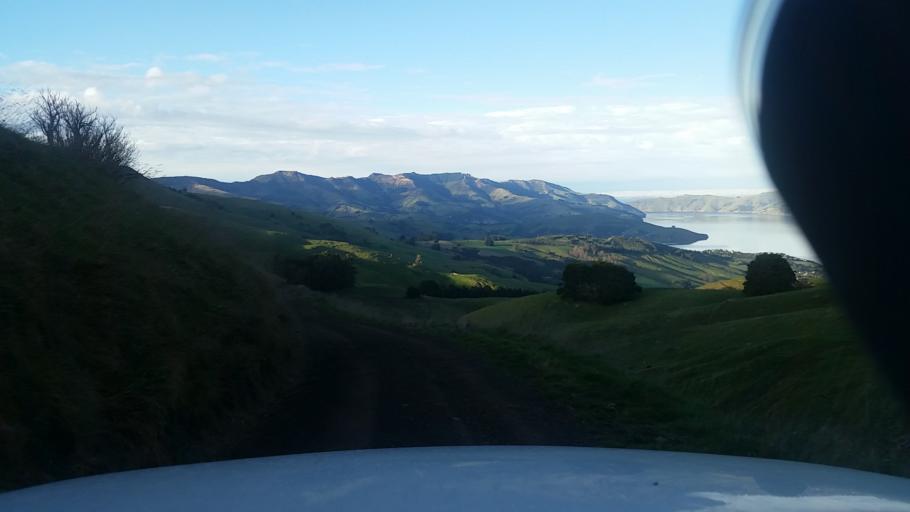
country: NZ
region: Canterbury
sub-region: Christchurch City
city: Christchurch
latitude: -43.7265
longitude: 172.9577
